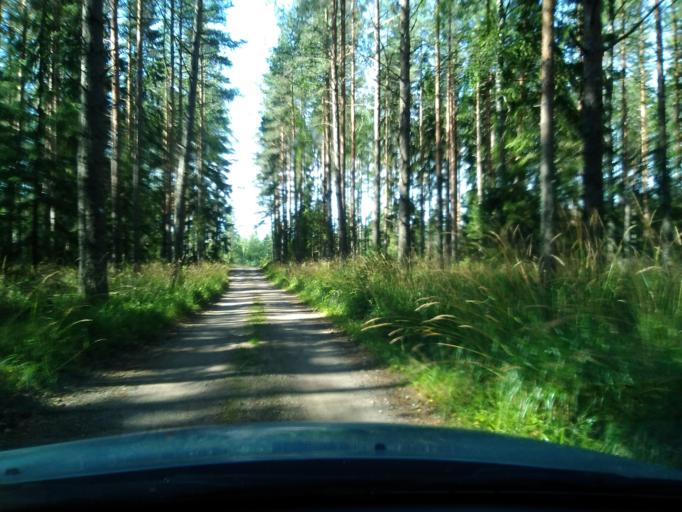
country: FI
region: Uusimaa
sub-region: Helsinki
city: Kaerkoelae
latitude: 60.7300
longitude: 24.0734
